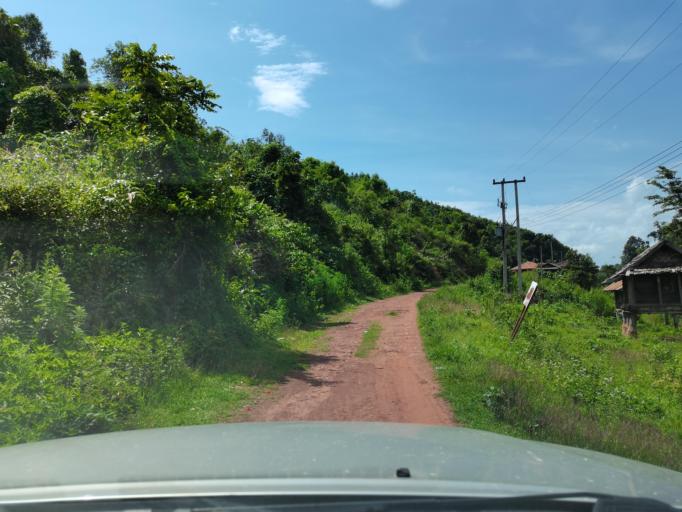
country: LA
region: Loungnamtha
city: Muang Nale
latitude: 20.5279
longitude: 101.0651
